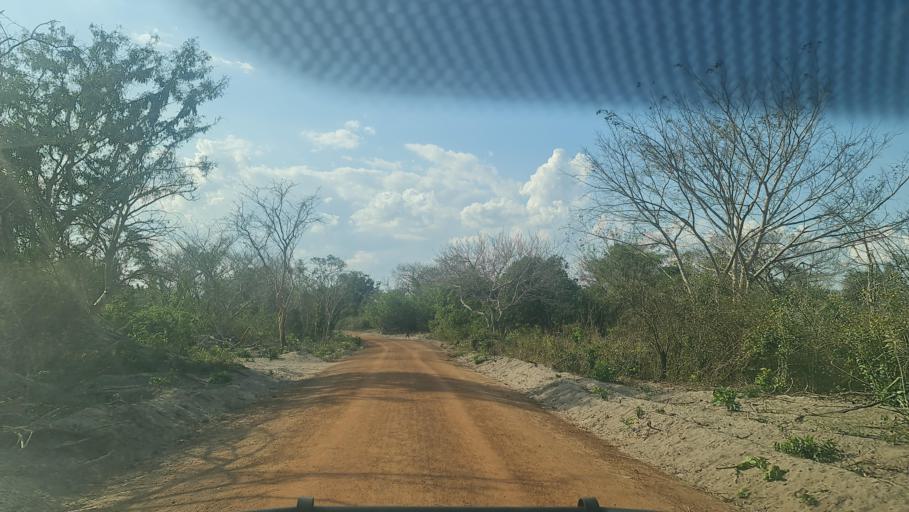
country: MZ
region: Nampula
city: Ilha de Mocambique
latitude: -15.5025
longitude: 40.1620
